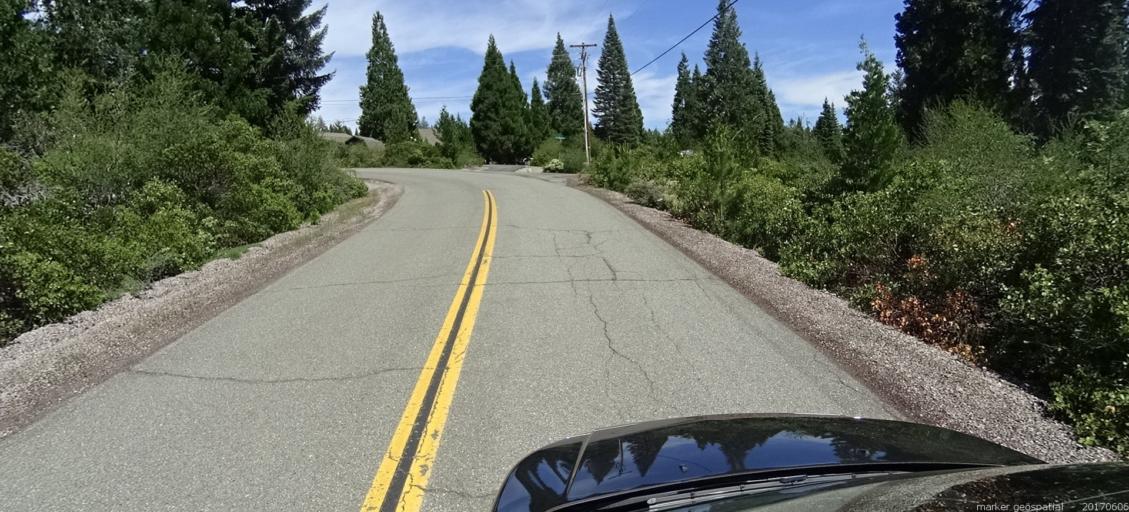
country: US
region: California
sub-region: Siskiyou County
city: Mount Shasta
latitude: 41.2837
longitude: -122.2921
